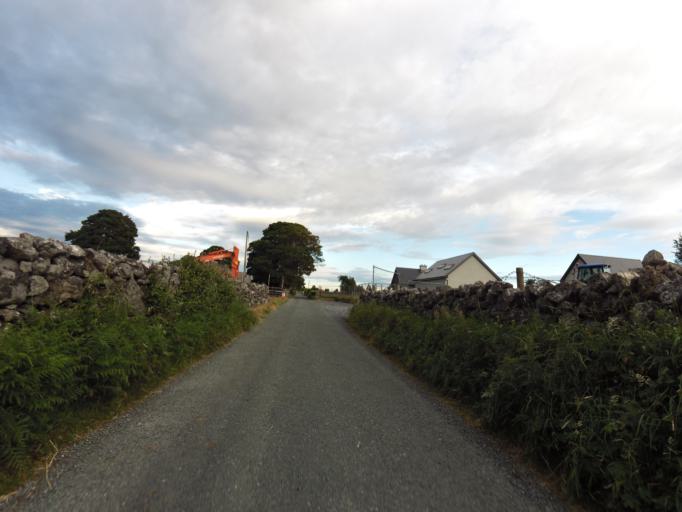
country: IE
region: Connaught
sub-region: County Galway
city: Athenry
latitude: 53.2938
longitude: -8.7248
